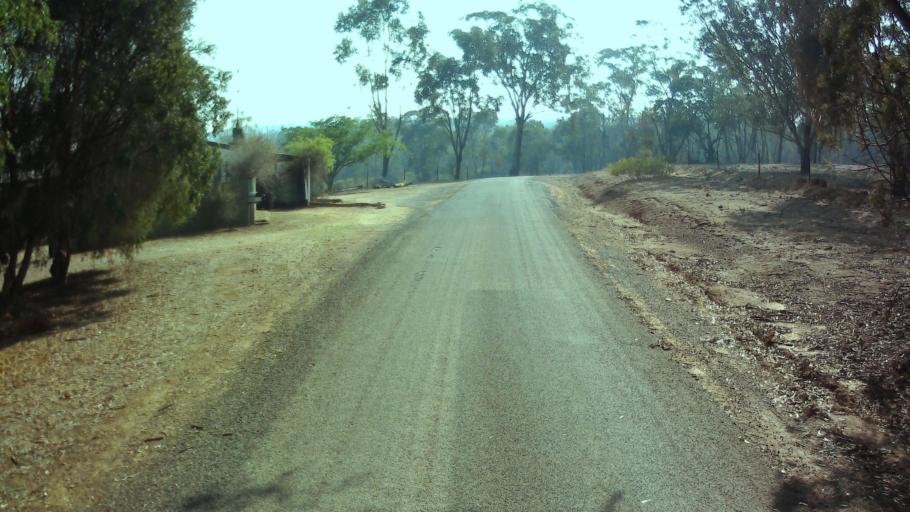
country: AU
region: New South Wales
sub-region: Weddin
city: Grenfell
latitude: -33.8931
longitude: 148.1782
